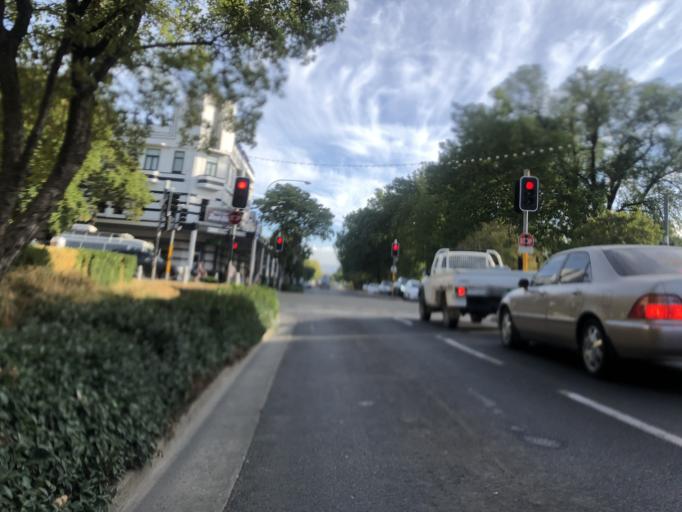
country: AU
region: New South Wales
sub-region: Orange Municipality
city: Orange
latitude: -33.2840
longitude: 149.1010
